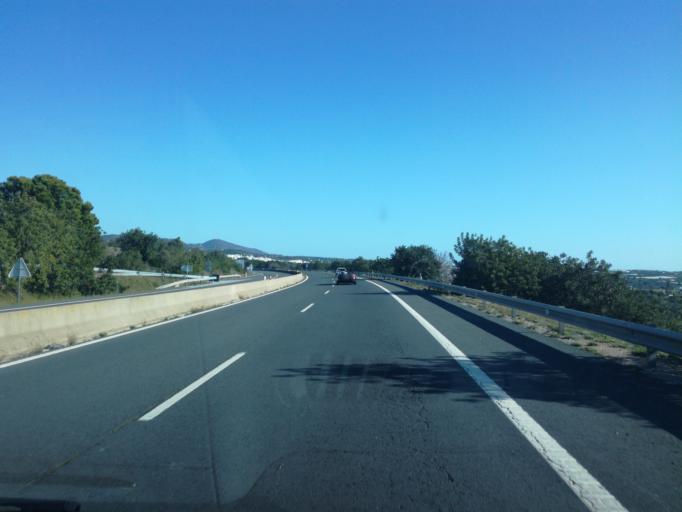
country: PT
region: Faro
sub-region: Faro
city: Santa Barbara de Nexe
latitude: 37.0925
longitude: -7.9267
